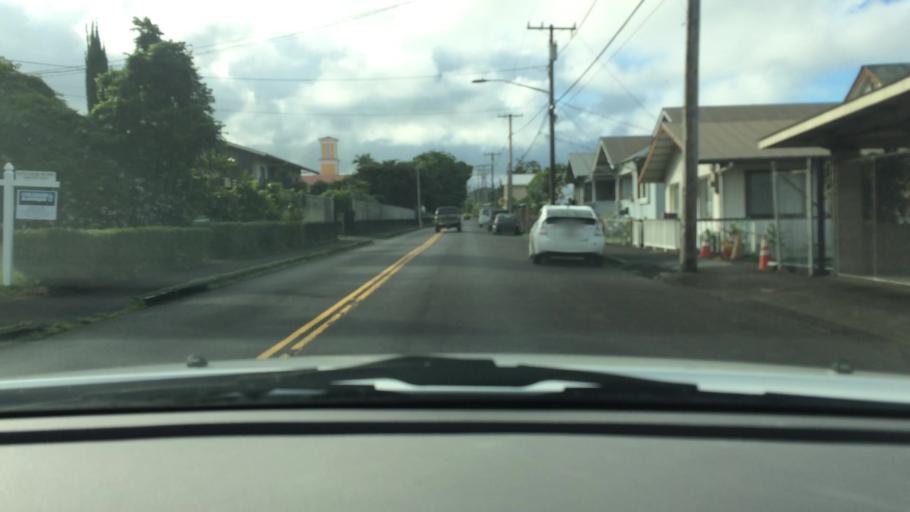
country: US
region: Hawaii
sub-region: Hawaii County
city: Hilo
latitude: 19.7208
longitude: -155.0876
